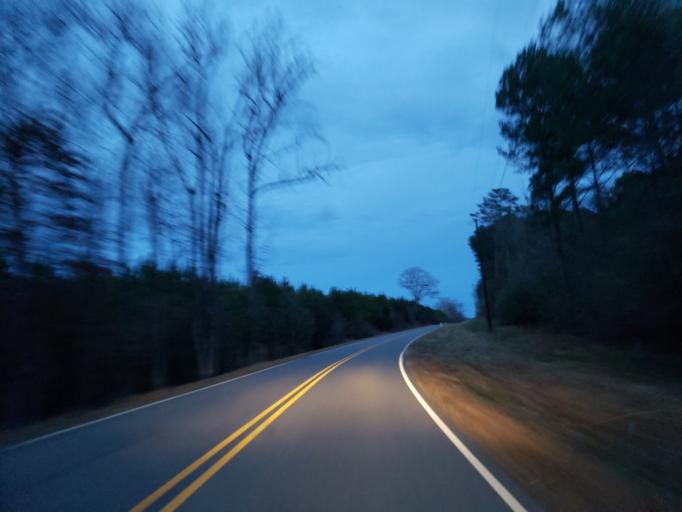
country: US
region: Alabama
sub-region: Greene County
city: Eutaw
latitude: 32.9033
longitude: -88.0256
